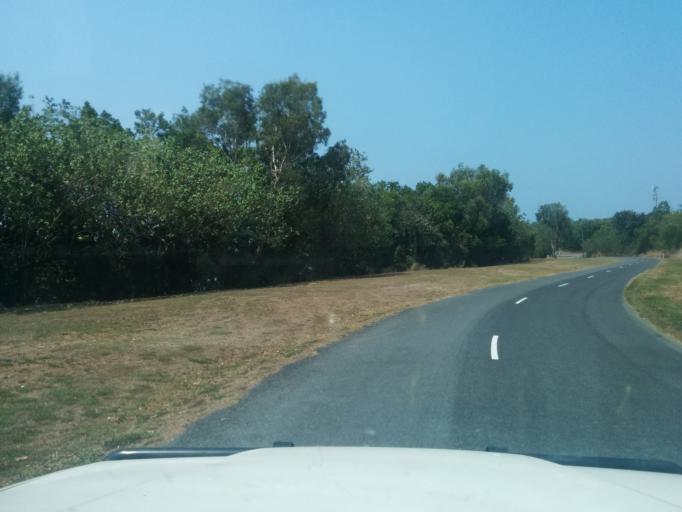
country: AU
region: Queensland
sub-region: Cairns
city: Redlynch
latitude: -16.8724
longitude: 145.7353
